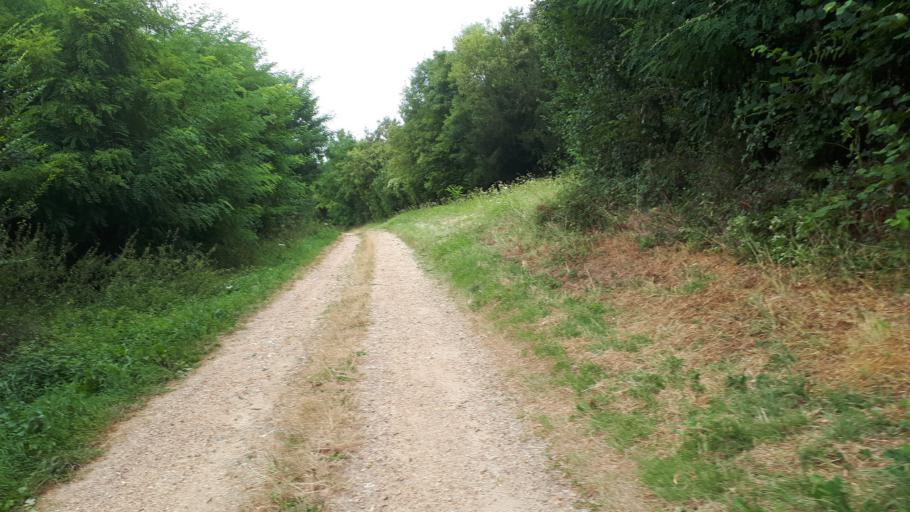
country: FR
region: Centre
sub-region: Departement du Loir-et-Cher
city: Villiers-sur-Loir
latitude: 47.8272
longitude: 0.9837
